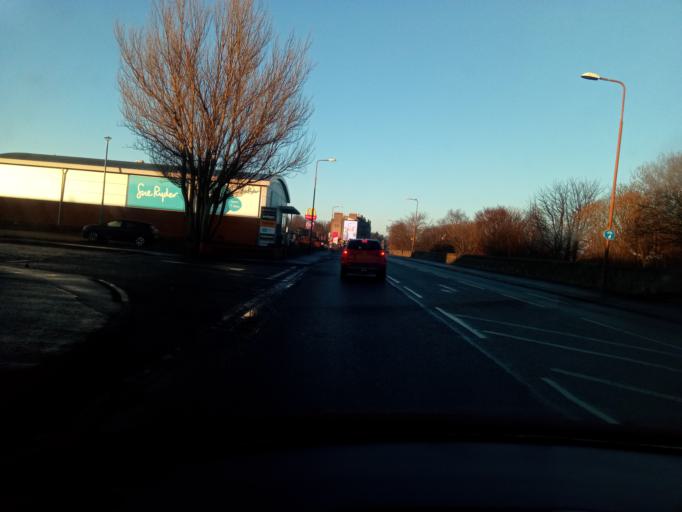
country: GB
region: Scotland
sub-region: West Lothian
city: Seafield
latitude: 55.9687
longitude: -3.1406
